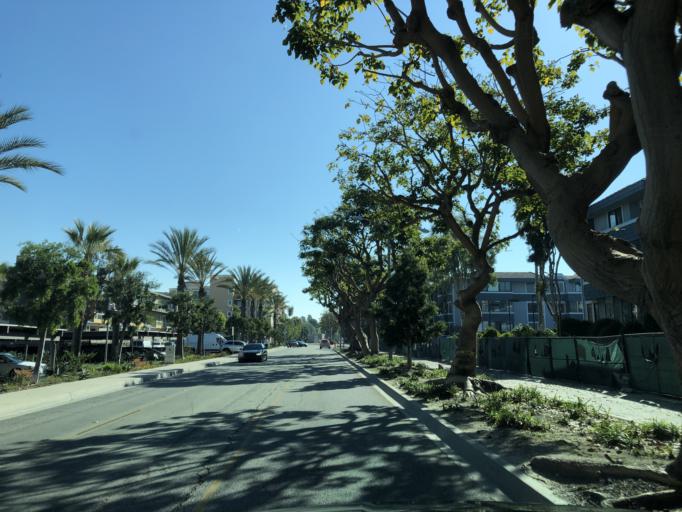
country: US
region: California
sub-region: Los Angeles County
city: Marina del Rey
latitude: 33.9727
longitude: -118.4567
